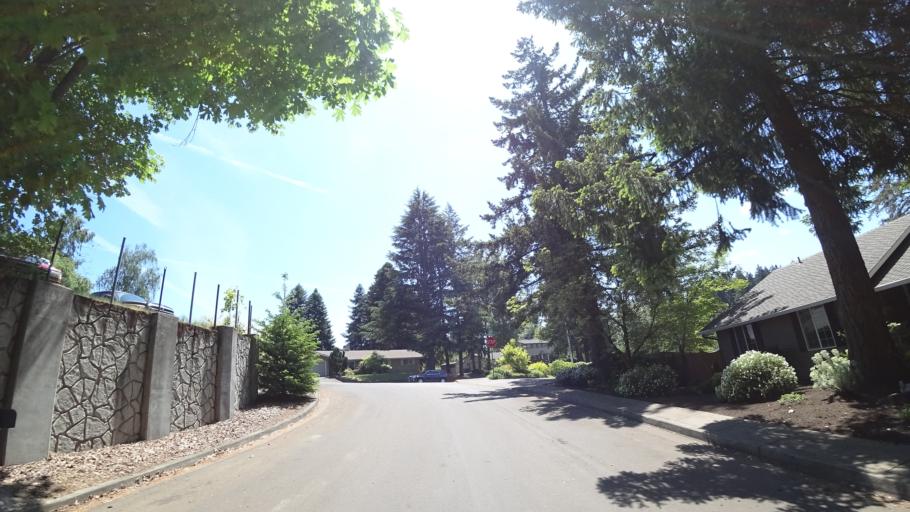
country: US
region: Oregon
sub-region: Washington County
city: King City
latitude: 45.4297
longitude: -122.8014
